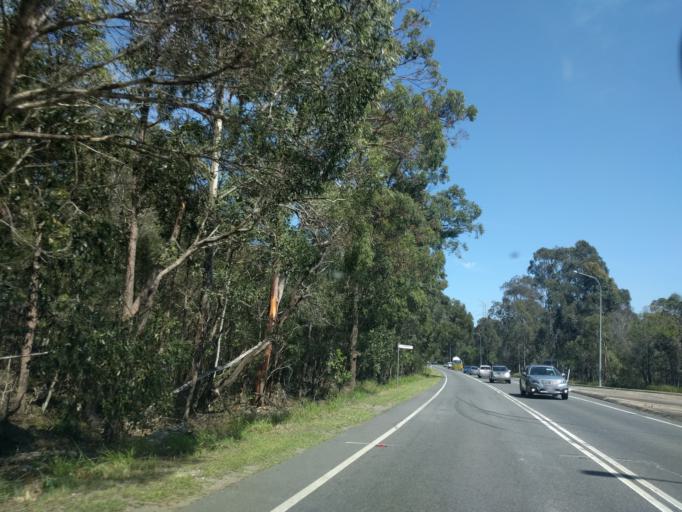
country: AU
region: Queensland
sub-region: Brisbane
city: Forest Lake
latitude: -27.6381
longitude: 152.9720
